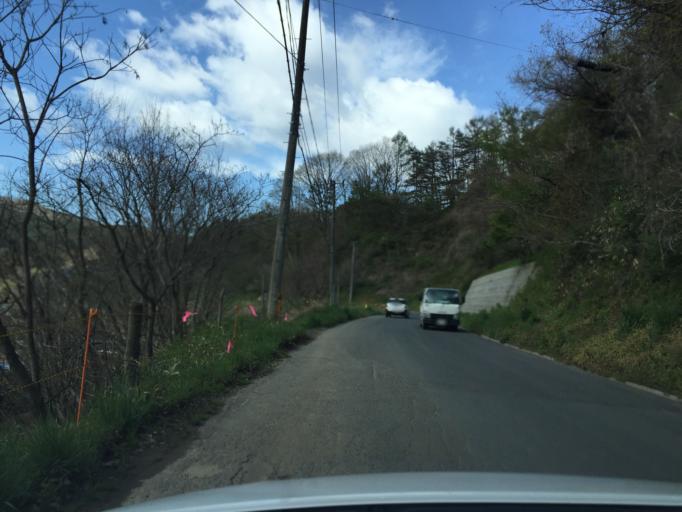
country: JP
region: Fukushima
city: Funehikimachi-funehiki
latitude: 37.5841
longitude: 140.6911
